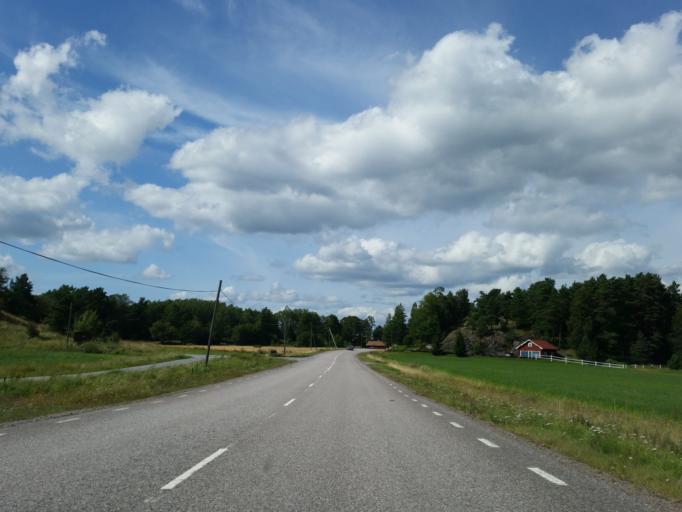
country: SE
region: Soedermanland
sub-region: Trosa Kommun
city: Vagnharad
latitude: 58.9987
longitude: 17.6072
